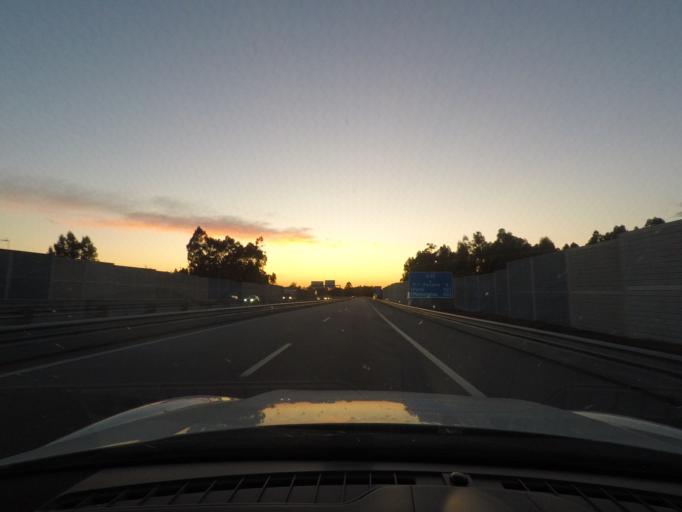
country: PT
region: Porto
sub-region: Pacos de Ferreira
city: Ferreira
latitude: 41.2599
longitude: -8.3390
